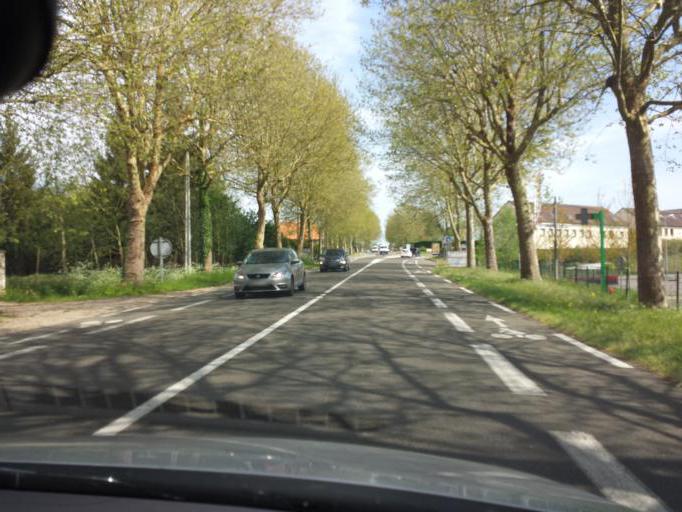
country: FR
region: Ile-de-France
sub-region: Departement des Yvelines
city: Villiers-Saint-Frederic
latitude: 48.8060
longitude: 1.8914
